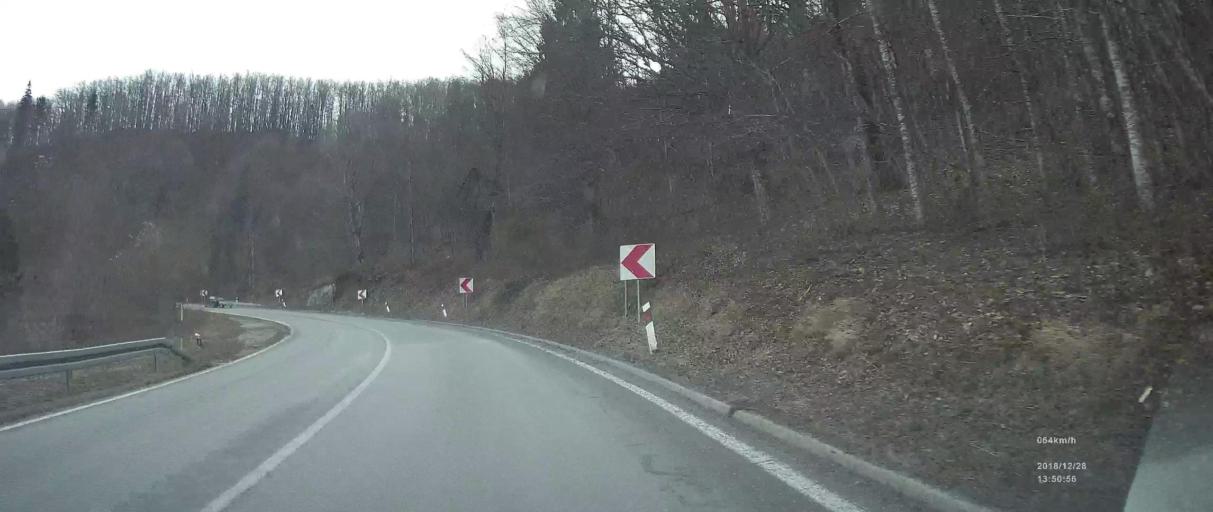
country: HR
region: Primorsko-Goranska
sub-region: Grad Delnice
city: Delnice
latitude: 45.3932
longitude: 14.8351
